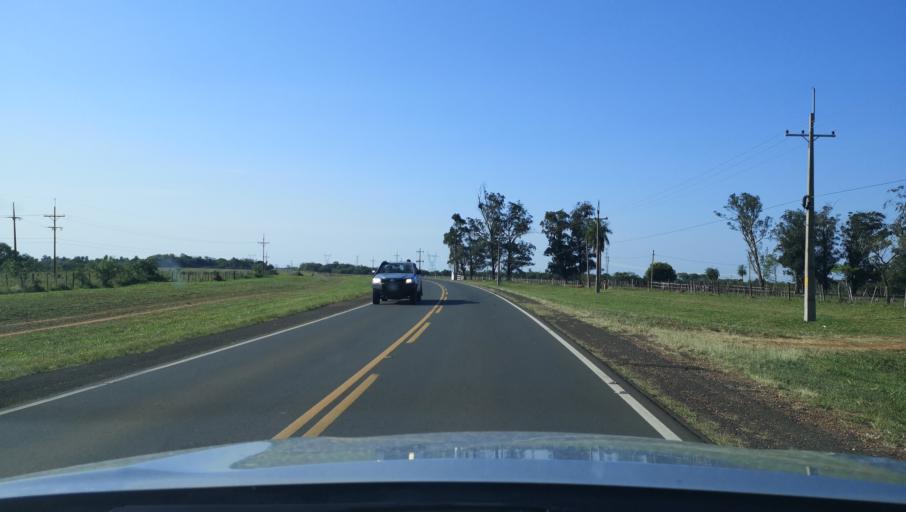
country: PY
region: Misiones
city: Santa Maria
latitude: -26.8070
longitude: -57.0200
